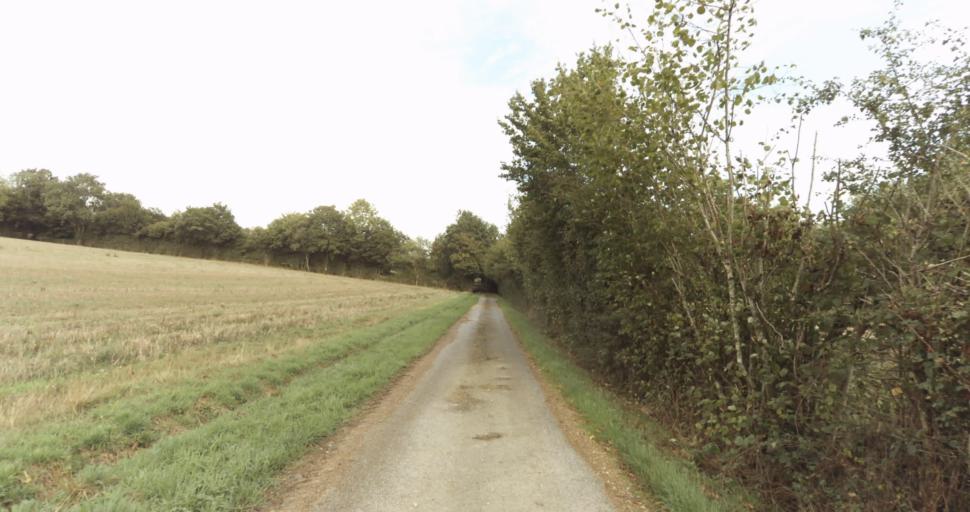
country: FR
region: Lower Normandy
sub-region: Departement de l'Orne
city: Sainte-Gauburge-Sainte-Colombe
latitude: 48.7066
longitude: 0.3637
